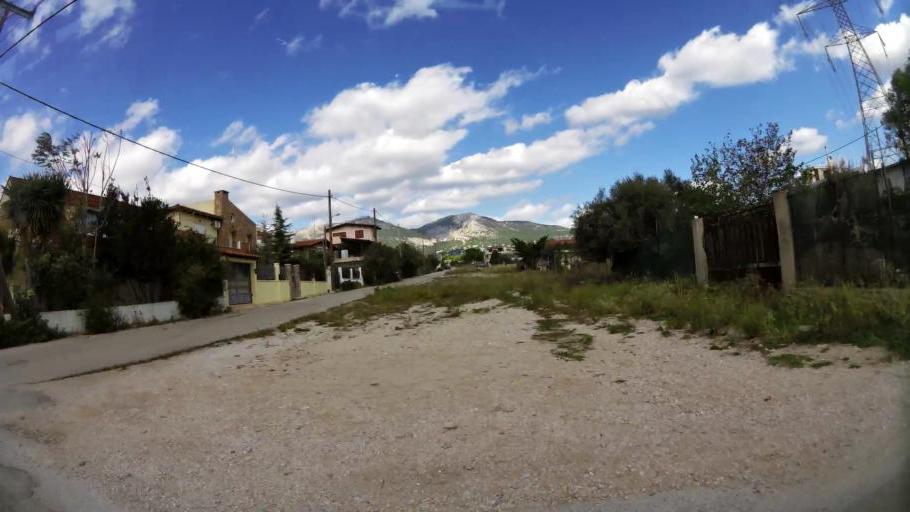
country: GR
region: Attica
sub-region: Nomarchia Anatolikis Attikis
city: Thrakomakedones
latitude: 38.1079
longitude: 23.7475
